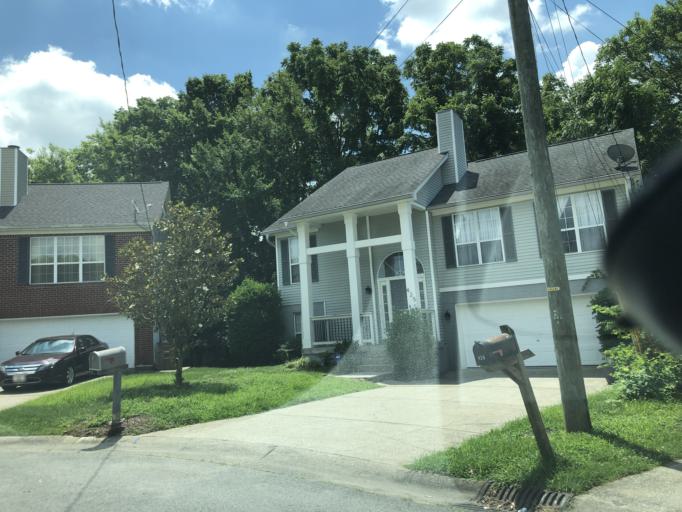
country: US
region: Tennessee
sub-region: Rutherford County
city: La Vergne
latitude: 36.0416
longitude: -86.6251
